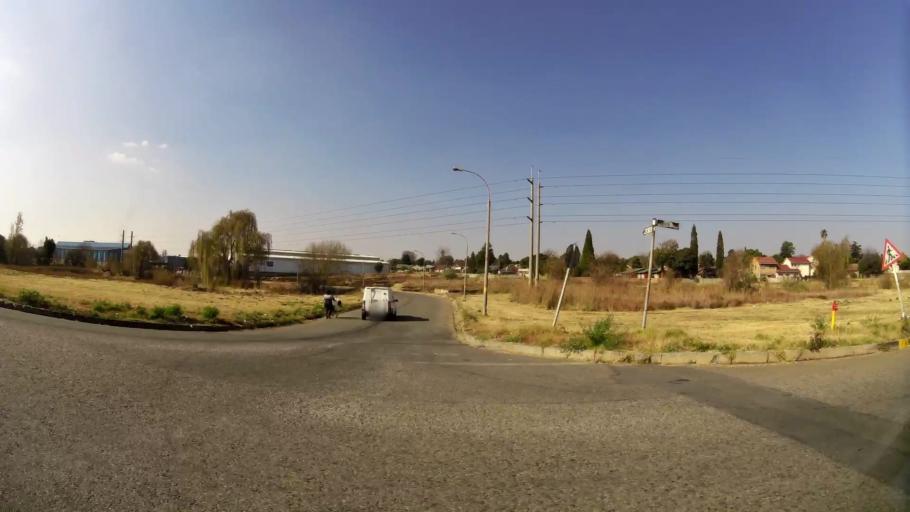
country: ZA
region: Gauteng
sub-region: City of Johannesburg Metropolitan Municipality
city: Modderfontein
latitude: -26.1181
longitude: 28.2225
